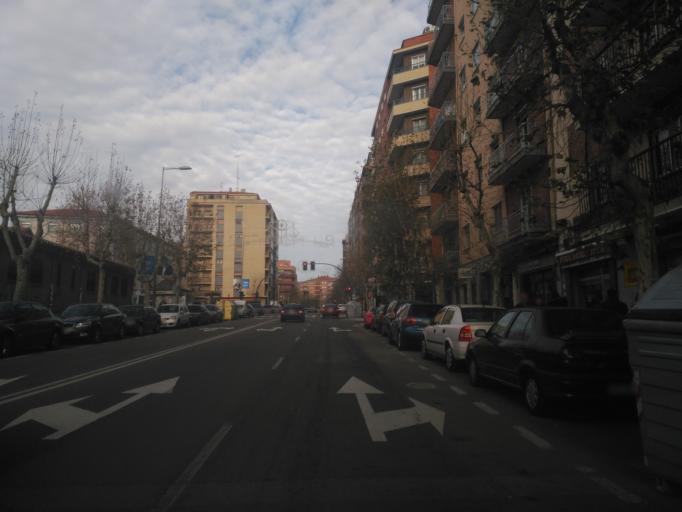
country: ES
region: Castille and Leon
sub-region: Provincia de Salamanca
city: Salamanca
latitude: 40.9707
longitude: -5.6702
